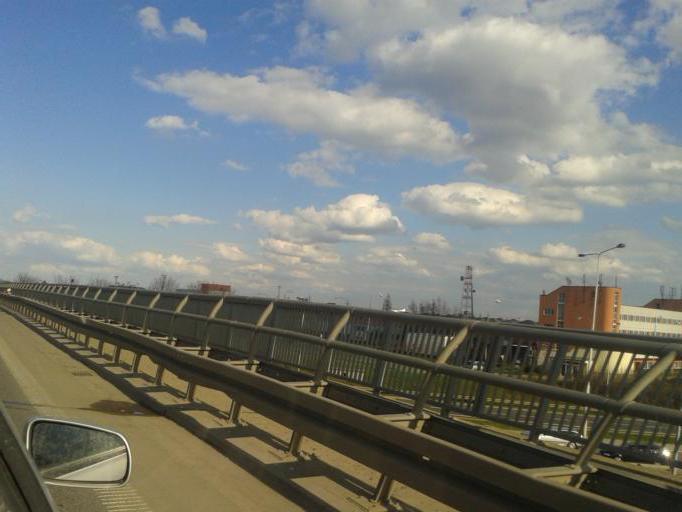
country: CZ
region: Central Bohemia
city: Hostivice
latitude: 50.0527
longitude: 14.2757
